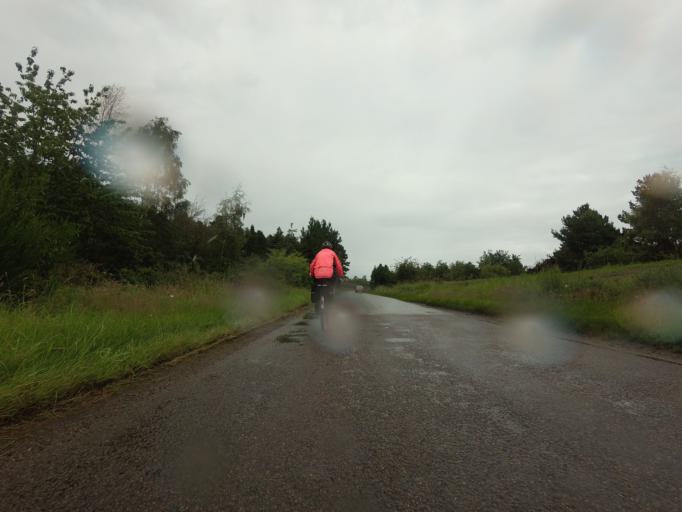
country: GB
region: Scotland
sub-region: Moray
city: Fochabers
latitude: 57.6604
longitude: -3.0669
